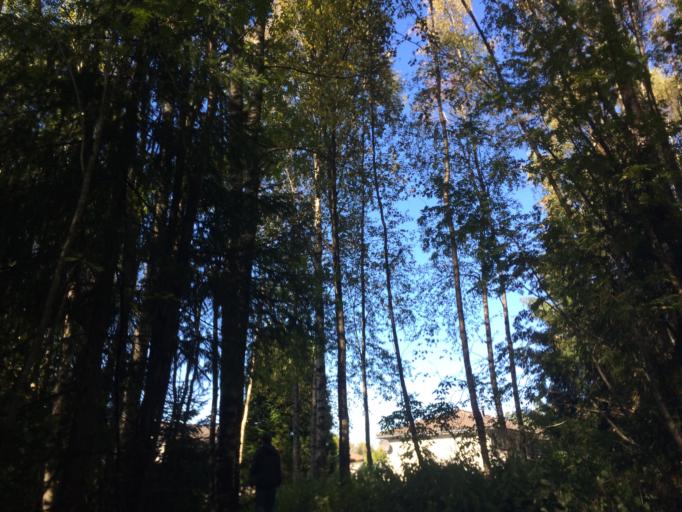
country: NO
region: Akershus
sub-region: Ski
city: Ski
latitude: 59.7172
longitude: 10.8100
